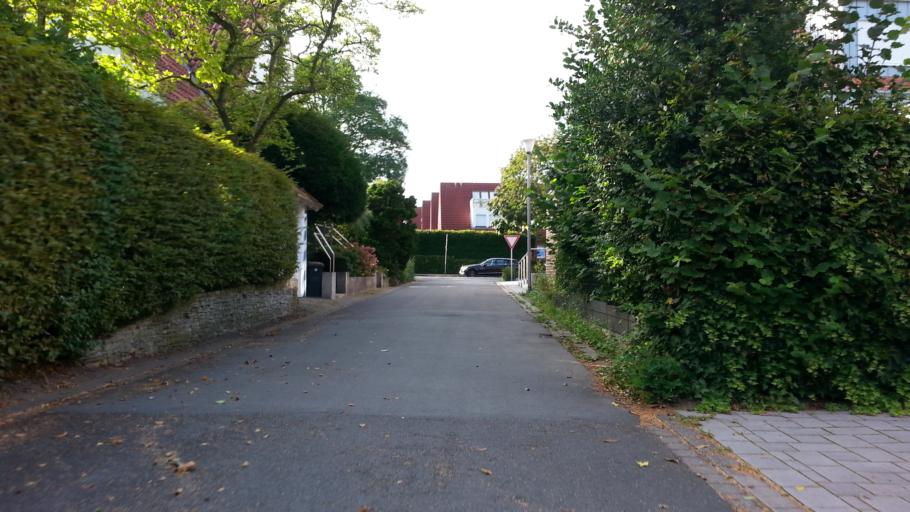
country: DE
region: North Rhine-Westphalia
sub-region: Regierungsbezirk Munster
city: Muenster
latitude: 51.9528
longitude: 7.5971
